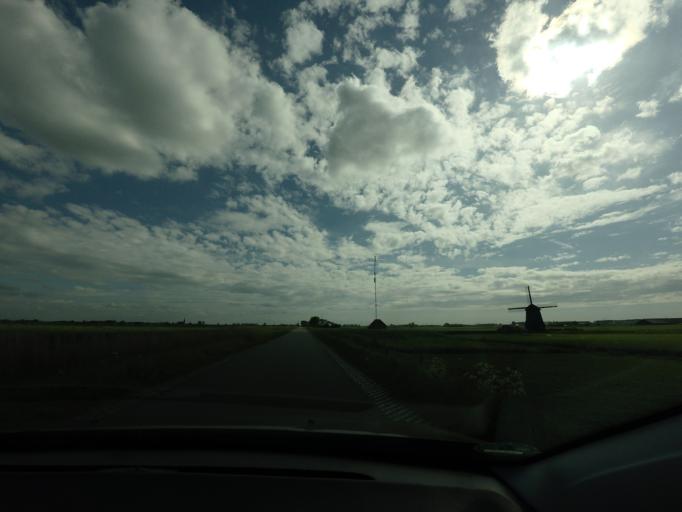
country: NL
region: North Holland
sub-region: Gemeente Heerhugowaard
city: Heerhugowaard
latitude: 52.6176
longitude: 4.8855
